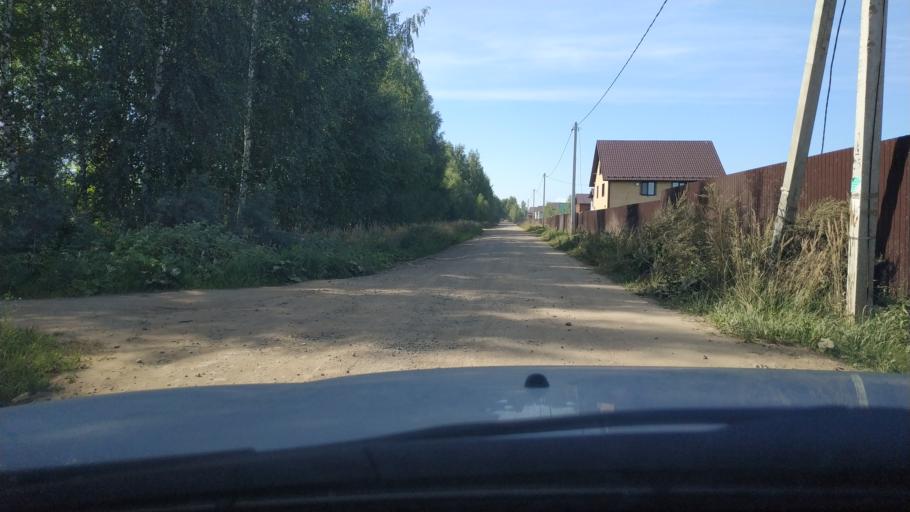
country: RU
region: Kostroma
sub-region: Kostromskoy Rayon
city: Kostroma
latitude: 57.7781
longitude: 40.7443
